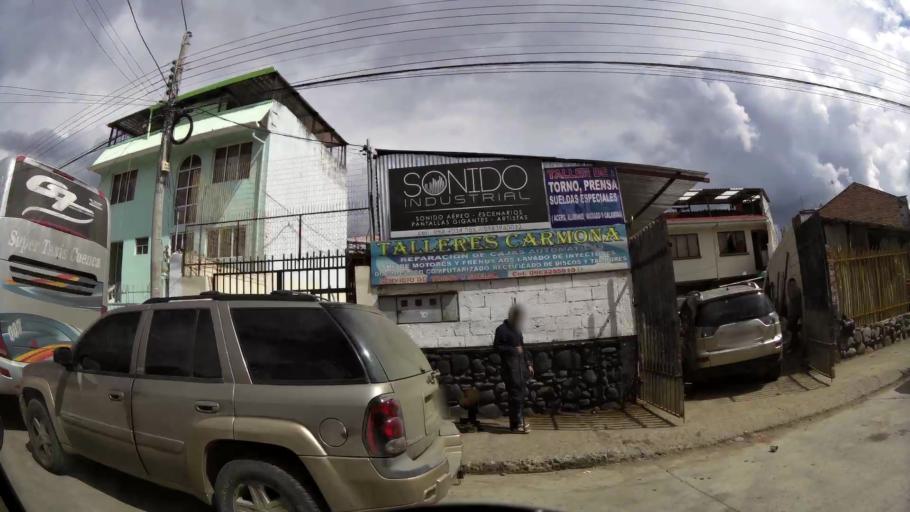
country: EC
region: Azuay
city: Cuenca
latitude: -2.8936
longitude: -78.9918
